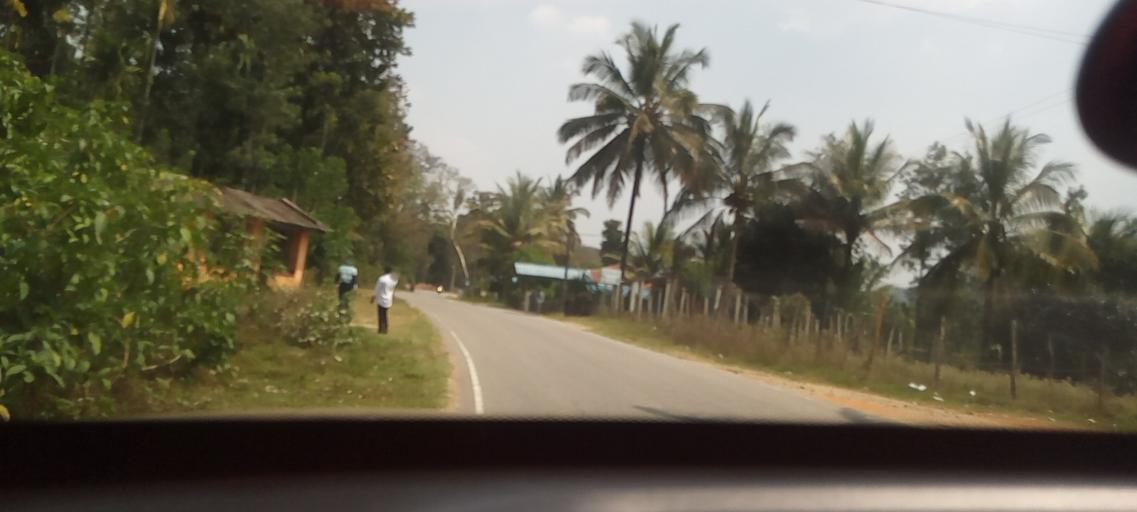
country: IN
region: Karnataka
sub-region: Chikmagalur
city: Mudigere
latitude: 13.2801
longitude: 75.6045
